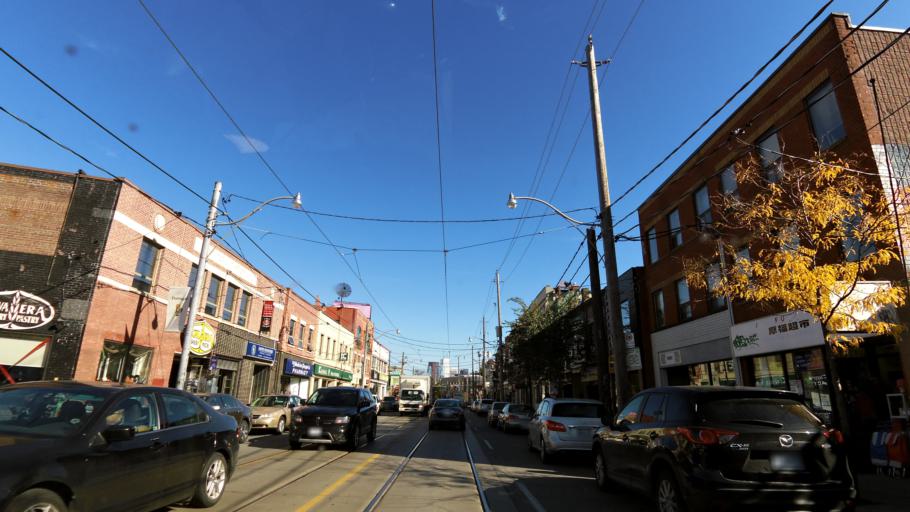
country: CA
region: Ontario
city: Toronto
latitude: 43.6494
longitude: -79.4224
